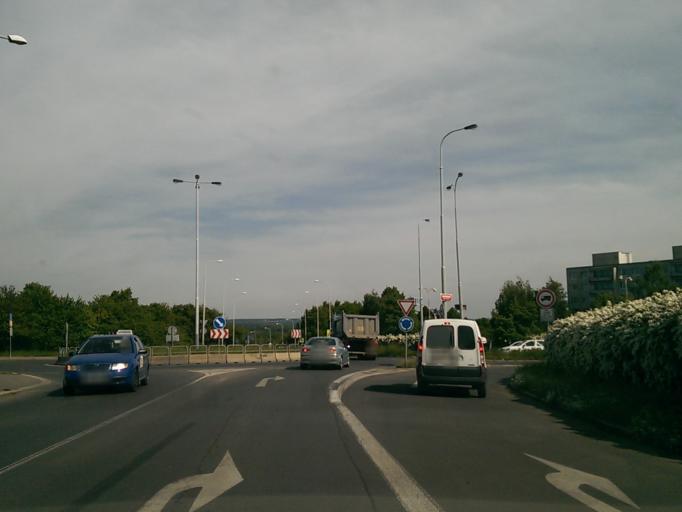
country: CZ
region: Central Bohemia
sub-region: Okres Praha-Zapad
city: Pruhonice
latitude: 50.0341
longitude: 14.5368
